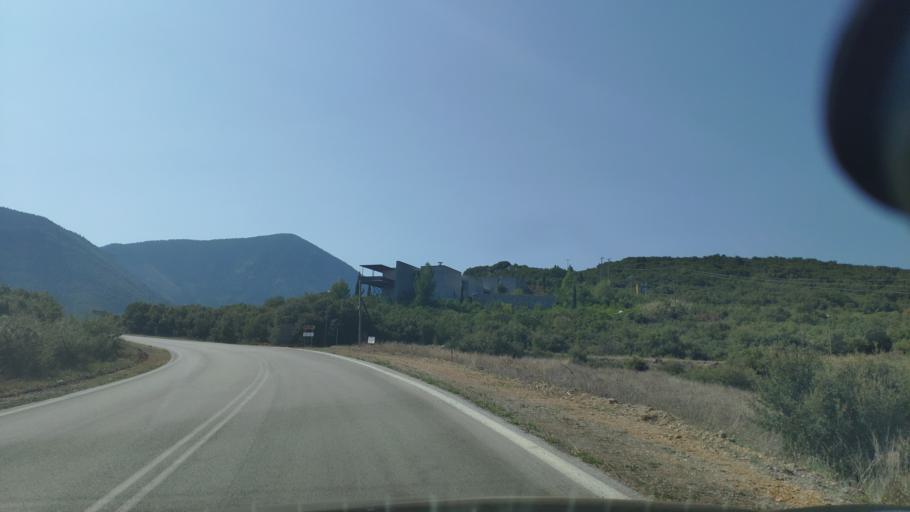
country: GR
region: Peloponnese
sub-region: Nomos Korinthias
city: Nemea
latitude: 37.8593
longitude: 22.4533
